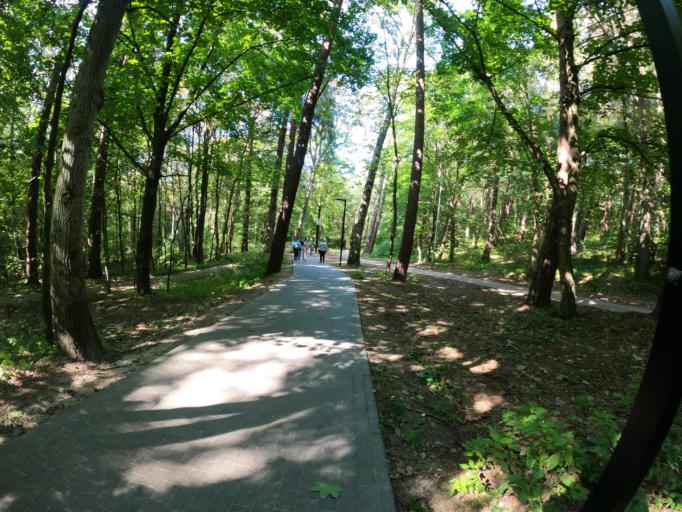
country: RU
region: Kaliningrad
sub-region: Gorod Svetlogorsk
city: Svetlogorsk
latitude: 54.9356
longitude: 20.1591
